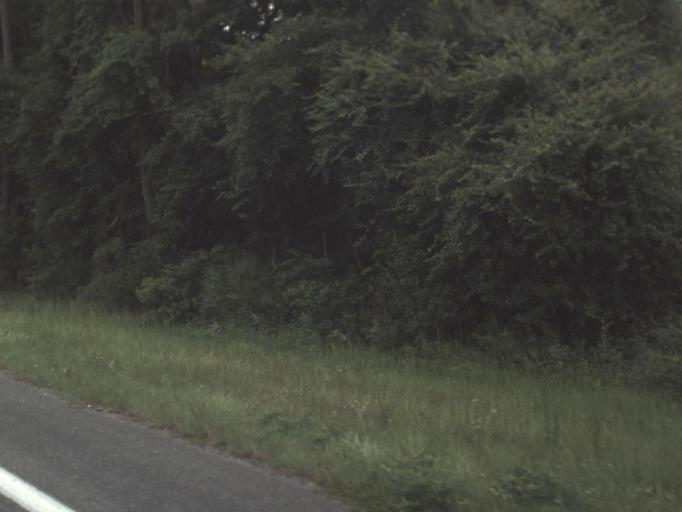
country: US
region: Florida
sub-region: Union County
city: Lake Butler
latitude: 30.0367
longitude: -82.3763
